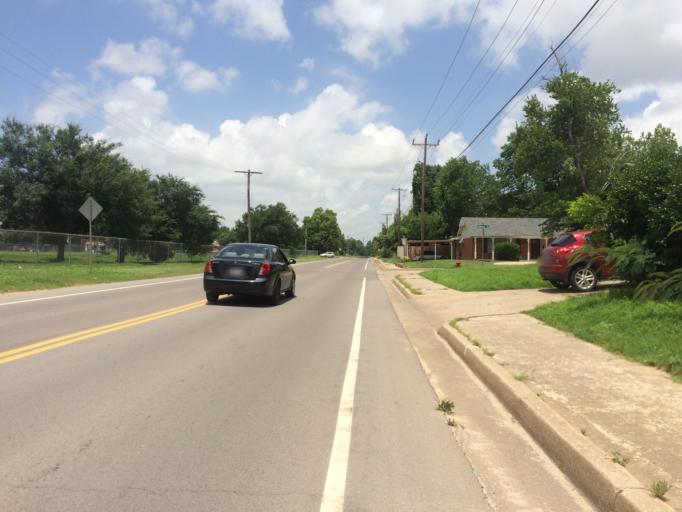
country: US
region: Oklahoma
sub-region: Cleveland County
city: Norman
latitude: 35.2058
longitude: -97.4677
